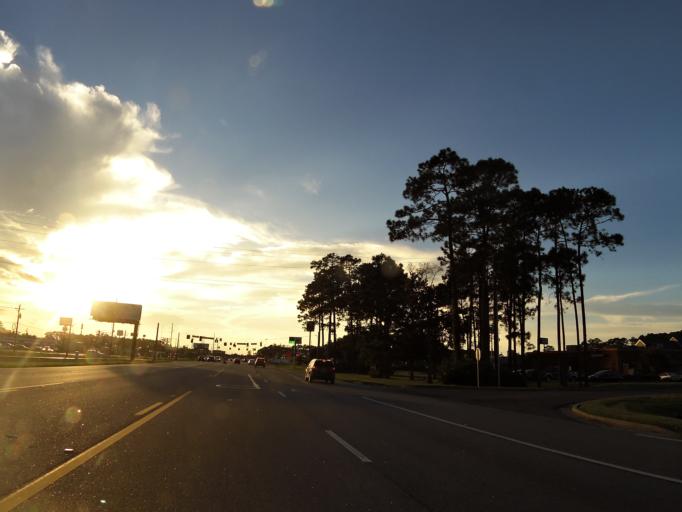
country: US
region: Georgia
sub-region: Camden County
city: Kingsland
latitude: 30.7881
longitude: -81.6507
